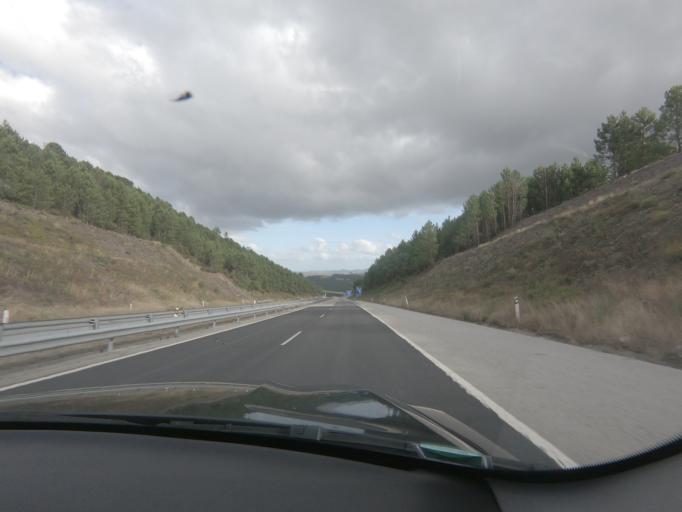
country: PT
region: Viseu
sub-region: Castro Daire
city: Castro Daire
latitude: 40.9199
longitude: -7.9163
